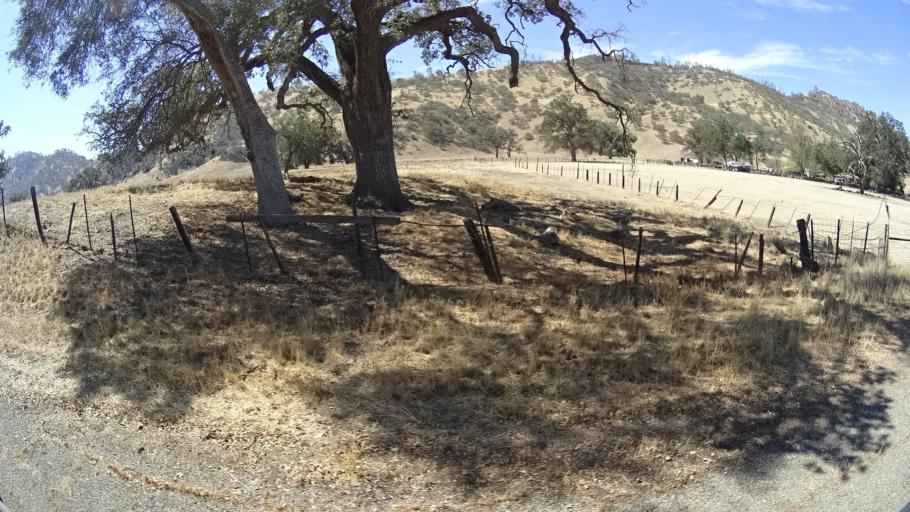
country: US
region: California
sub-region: San Luis Obispo County
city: San Miguel
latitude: 36.1333
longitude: -120.7455
